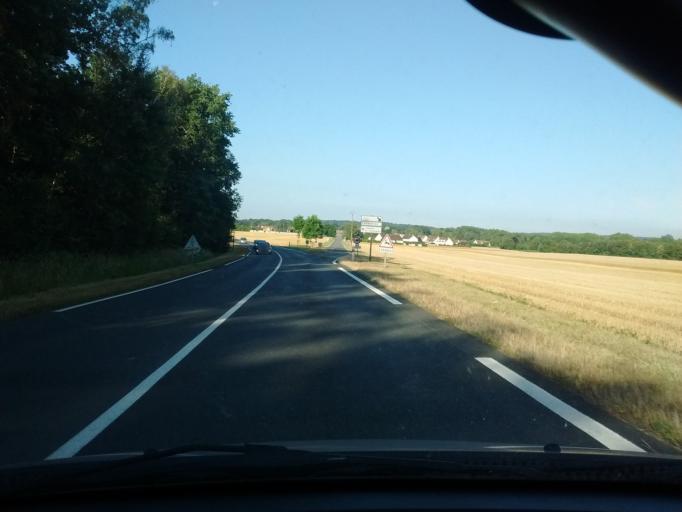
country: FR
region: Ile-de-France
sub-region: Departement de l'Essonne
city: Moigny-sur-Ecole
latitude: 48.4442
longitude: 2.4849
